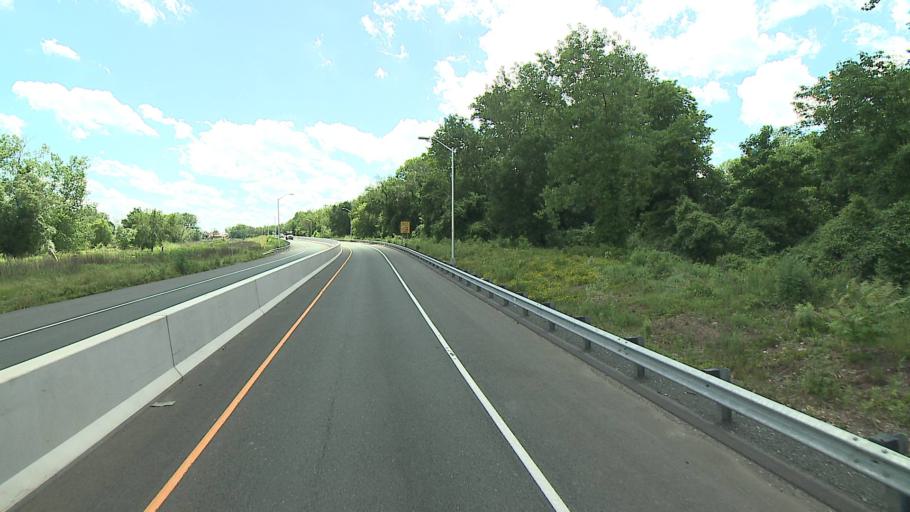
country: US
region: Connecticut
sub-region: Hartford County
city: Hartford
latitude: 41.7482
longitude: -72.7081
